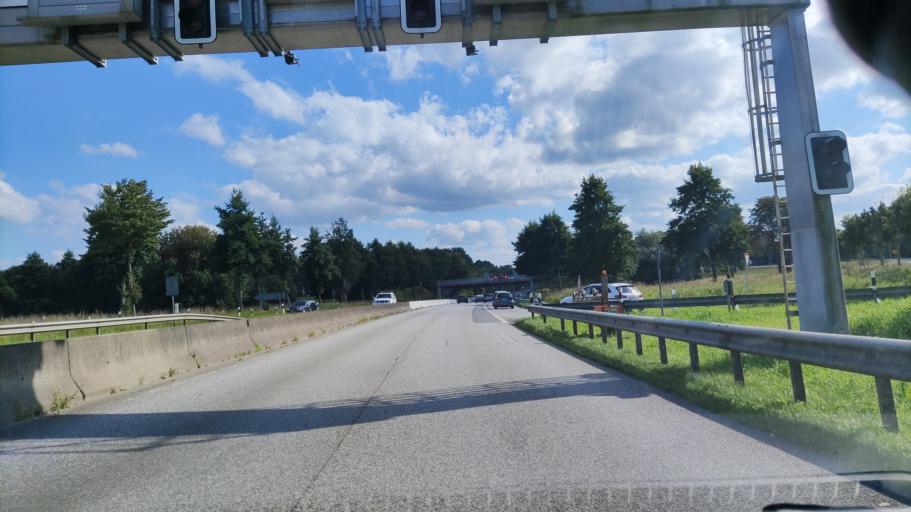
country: DE
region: Schleswig-Holstein
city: Westerronfeld
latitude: 54.2965
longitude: 9.6537
